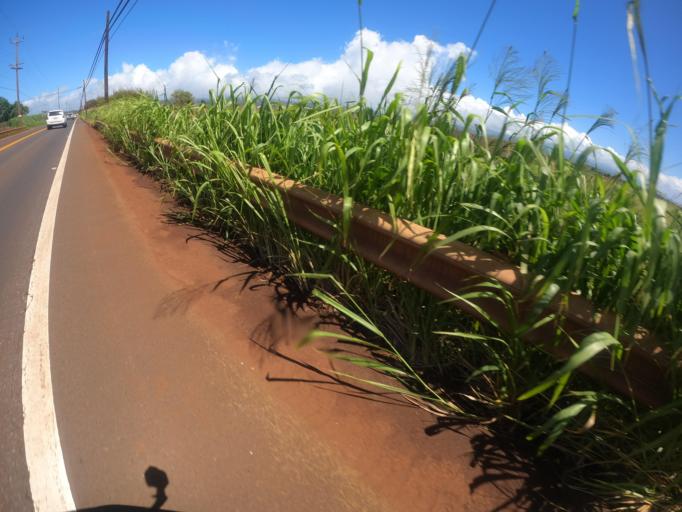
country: US
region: Hawaii
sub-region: Honolulu County
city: Schofield Barracks
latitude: 21.4624
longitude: -158.0562
